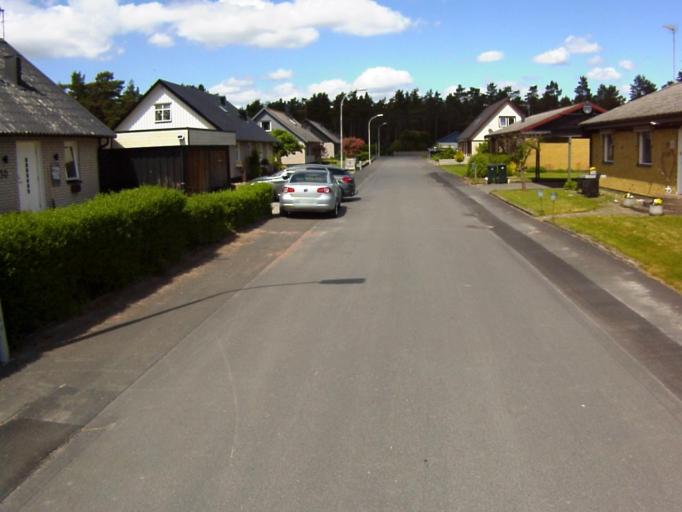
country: SE
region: Skane
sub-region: Kristianstads Kommun
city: Ahus
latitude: 55.9470
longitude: 14.2724
